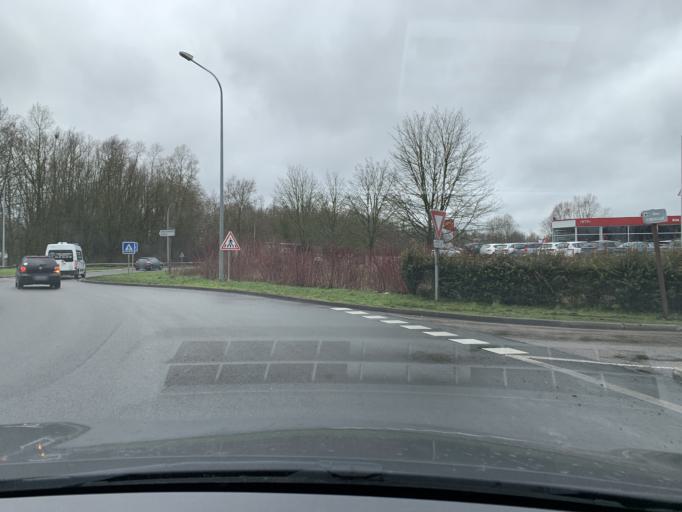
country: FR
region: Nord-Pas-de-Calais
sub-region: Departement du Nord
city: Sin-le-Noble
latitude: 50.3687
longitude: 3.1213
